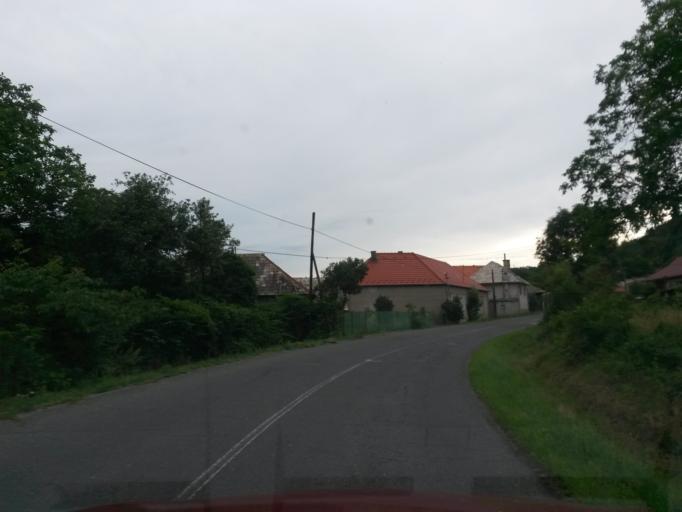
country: SK
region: Banskobystricky
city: Velky Krtis
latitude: 48.3126
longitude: 19.3995
